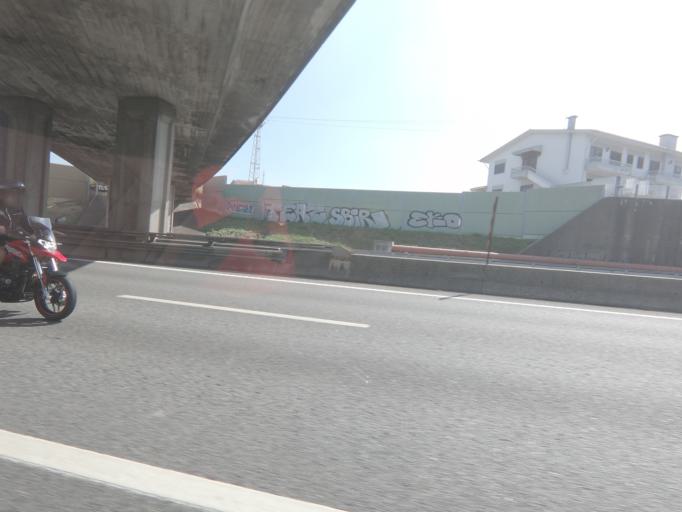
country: PT
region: Porto
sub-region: Maia
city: Pedroucos
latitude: 41.1865
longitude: -8.5945
